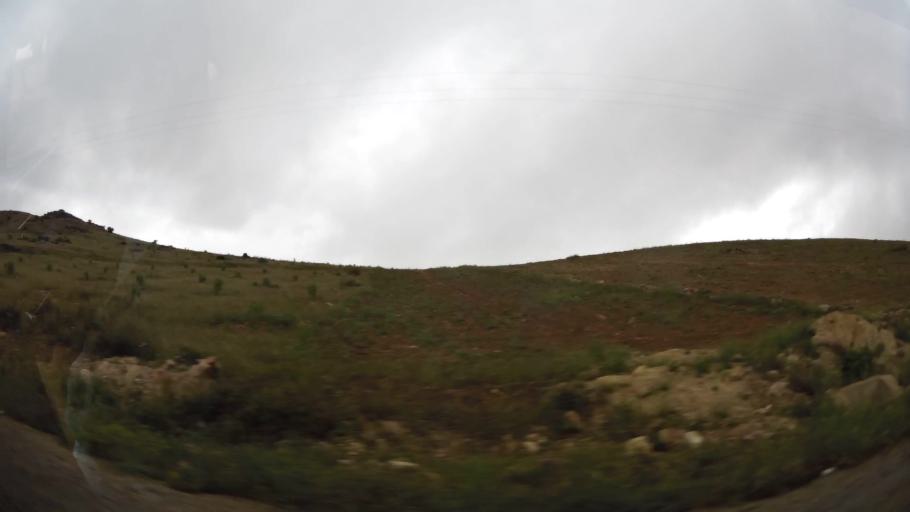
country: MA
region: Oriental
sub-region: Nador
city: Midar
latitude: 35.0668
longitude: -3.4750
